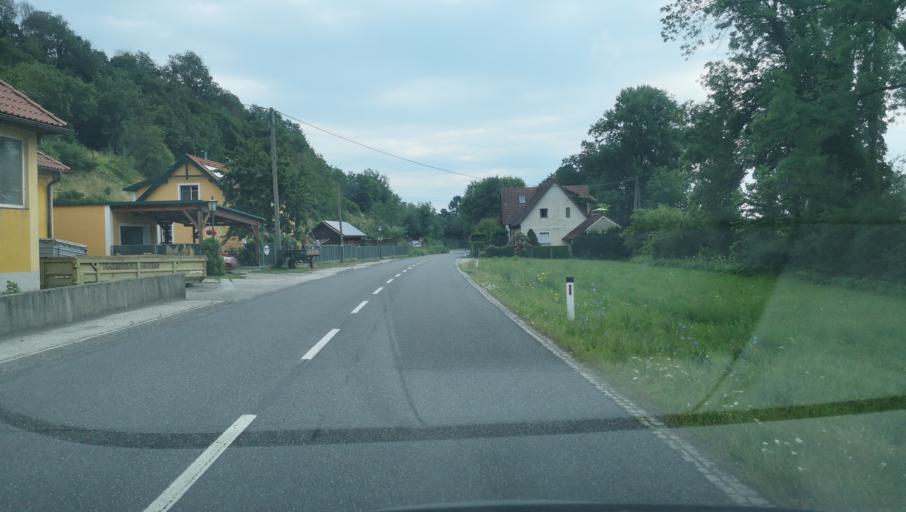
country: AT
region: Lower Austria
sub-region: Politischer Bezirk Melk
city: Leiben
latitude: 48.2300
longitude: 15.2990
